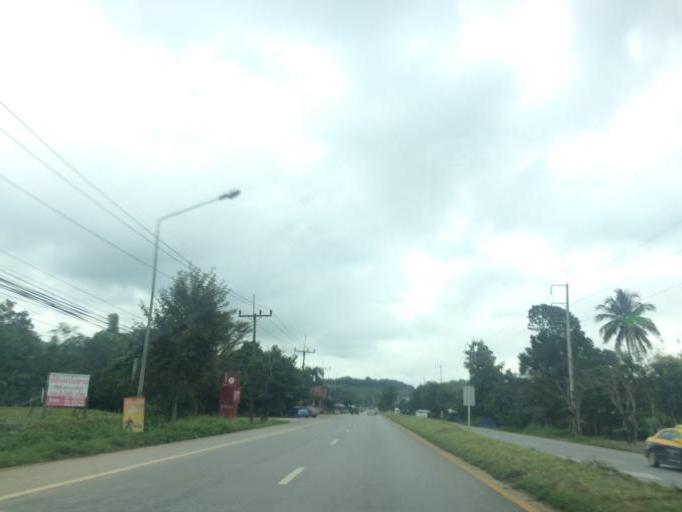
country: TH
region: Chiang Rai
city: Mae Chan
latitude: 20.1077
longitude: 99.8735
